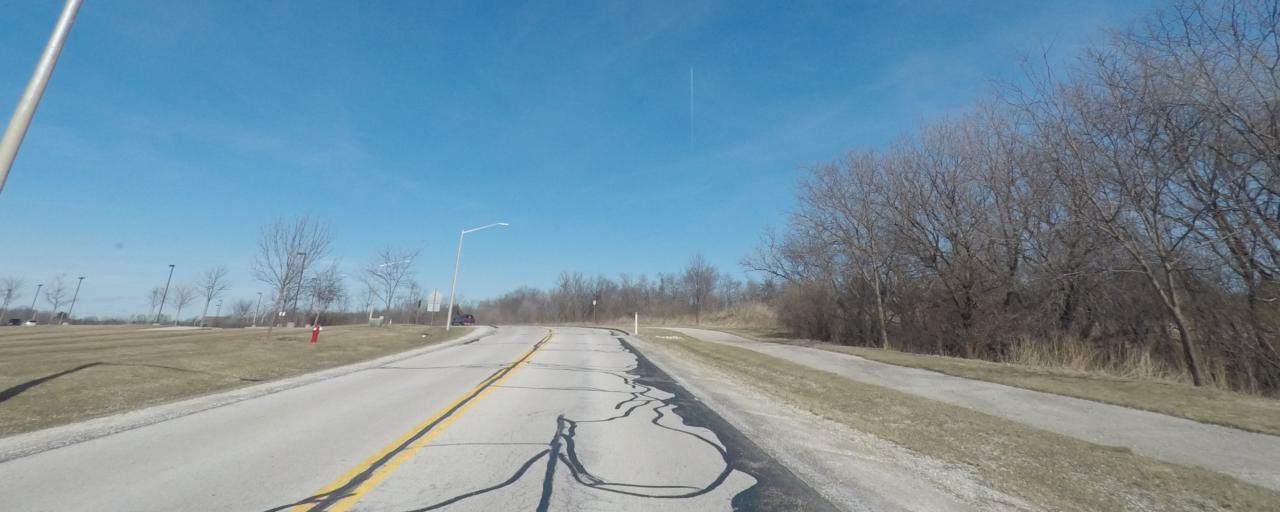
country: US
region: Wisconsin
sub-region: Waukesha County
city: Hartland
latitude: 43.1079
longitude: -88.3597
